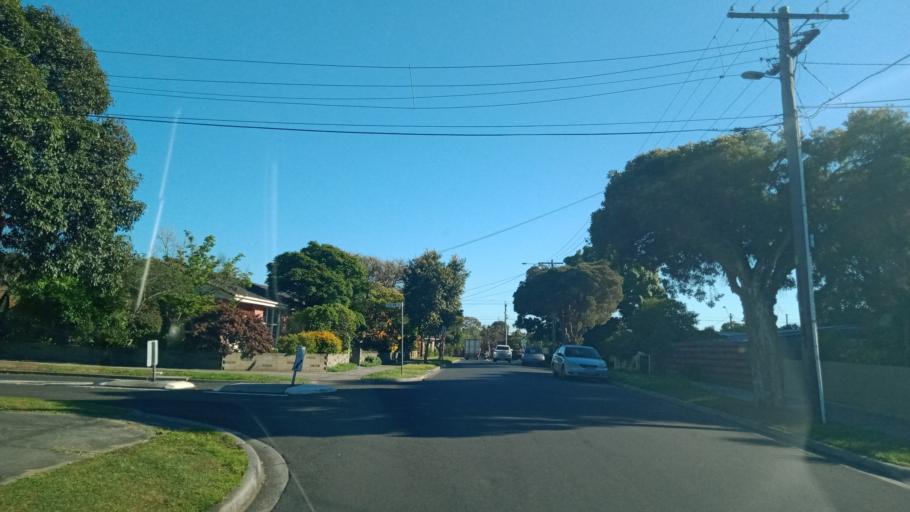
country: AU
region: Victoria
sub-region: Greater Dandenong
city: Noble Park North
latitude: -37.9362
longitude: 145.1736
